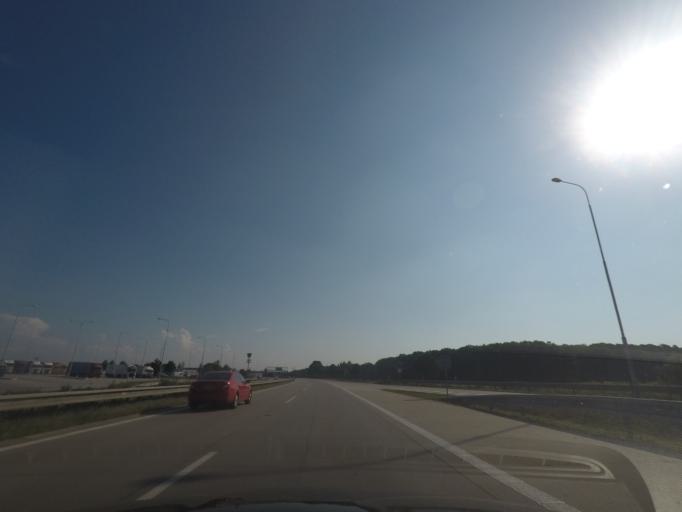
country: PL
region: Silesian Voivodeship
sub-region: Powiat raciborski
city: Chalupki
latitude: 49.9032
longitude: 18.3067
